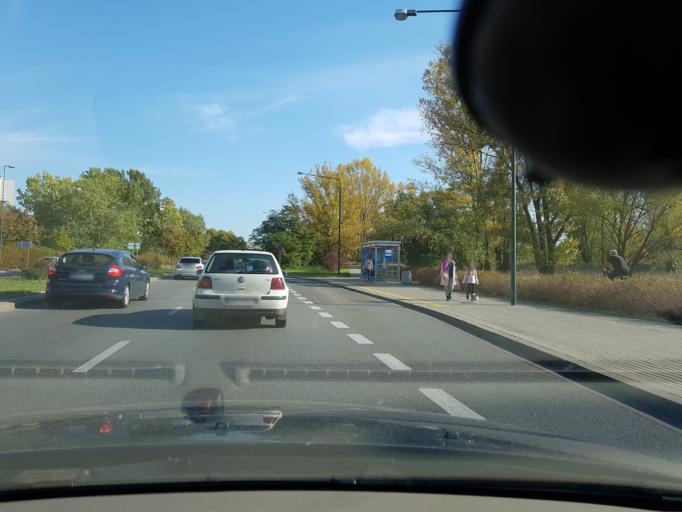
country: PL
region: Masovian Voivodeship
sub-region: Warszawa
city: Ursynow
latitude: 52.1549
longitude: 21.0503
